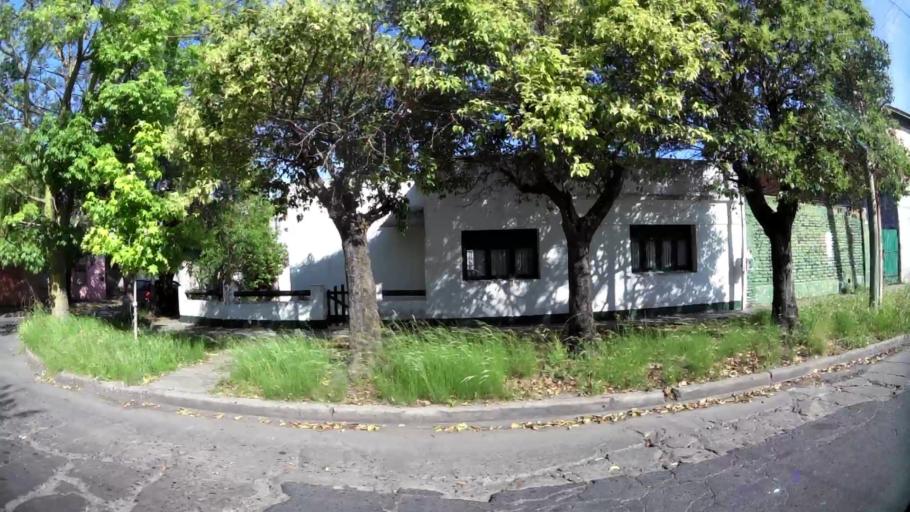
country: AR
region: Buenos Aires
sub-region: Partido de Moron
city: Moron
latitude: -34.6604
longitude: -58.5920
